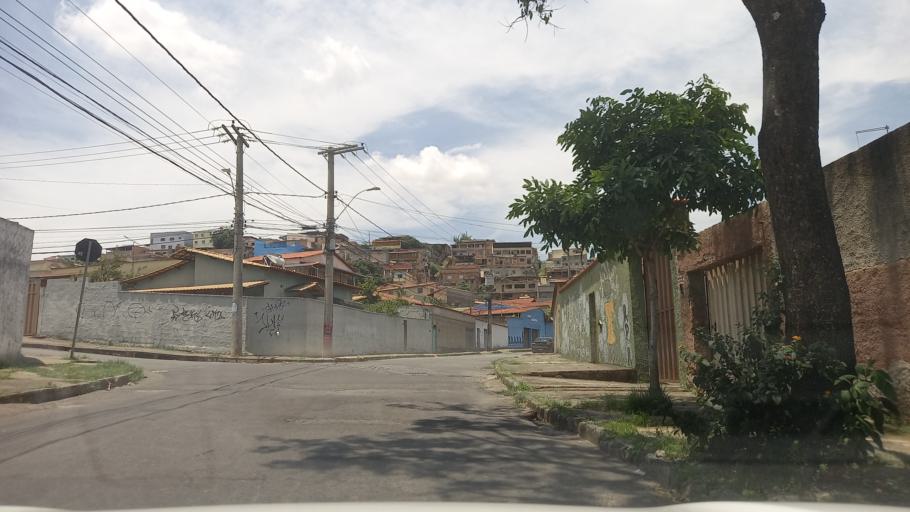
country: BR
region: Minas Gerais
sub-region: Contagem
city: Contagem
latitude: -19.9088
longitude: -44.0058
